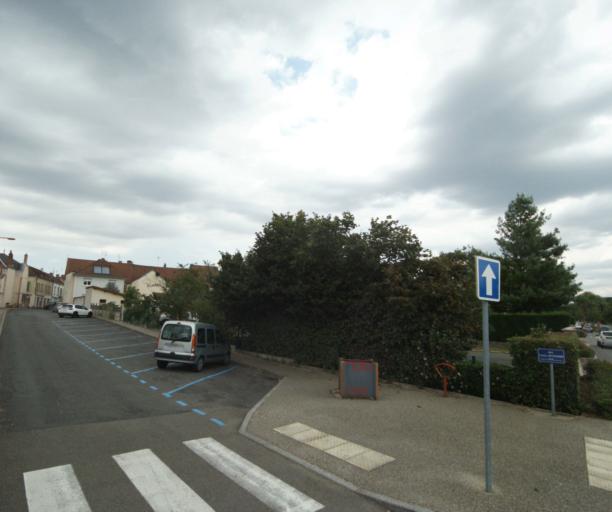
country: FR
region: Bourgogne
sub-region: Departement de Saone-et-Loire
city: Gueugnon
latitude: 46.5997
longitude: 4.0619
